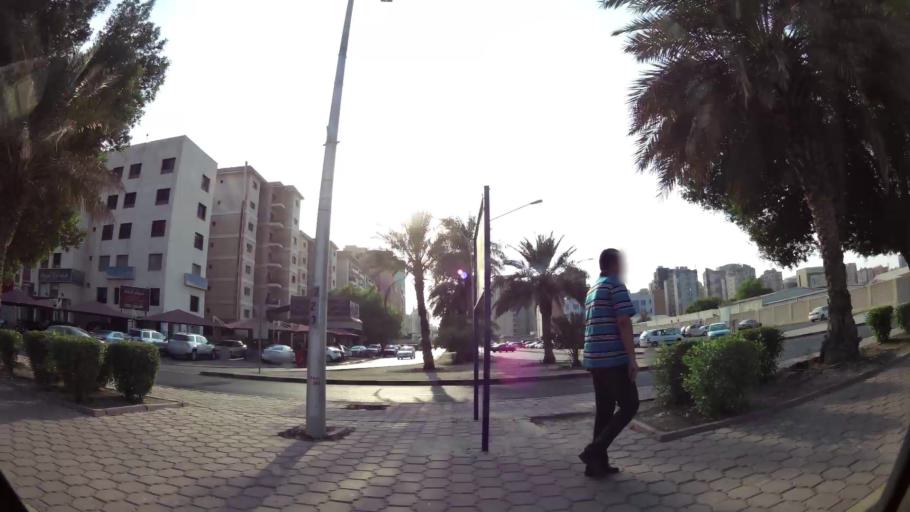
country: KW
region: Muhafazat Hawalli
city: Hawalli
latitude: 29.3245
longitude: 48.0307
